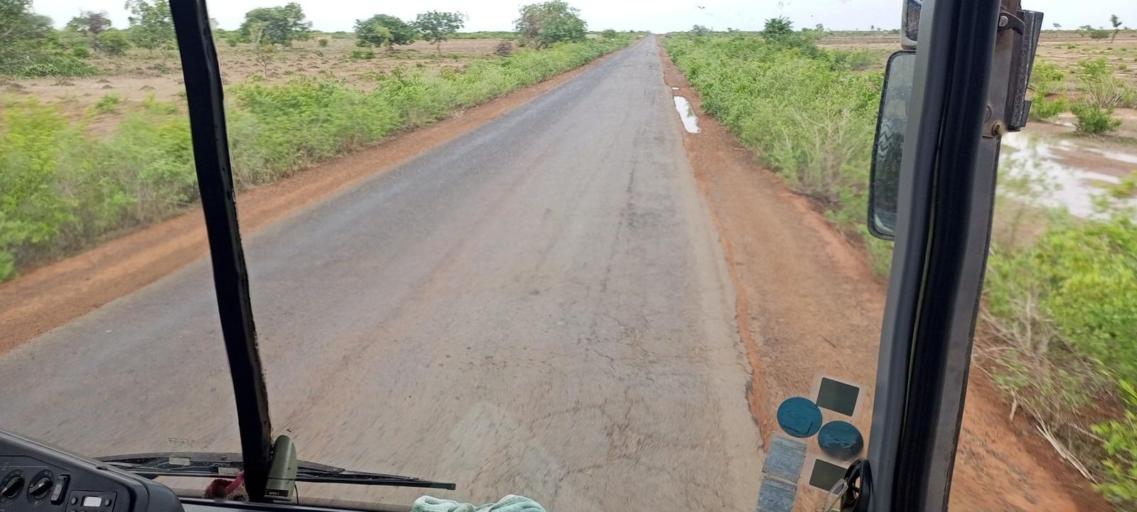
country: ML
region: Segou
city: Bla
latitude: 12.7099
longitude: -5.7244
